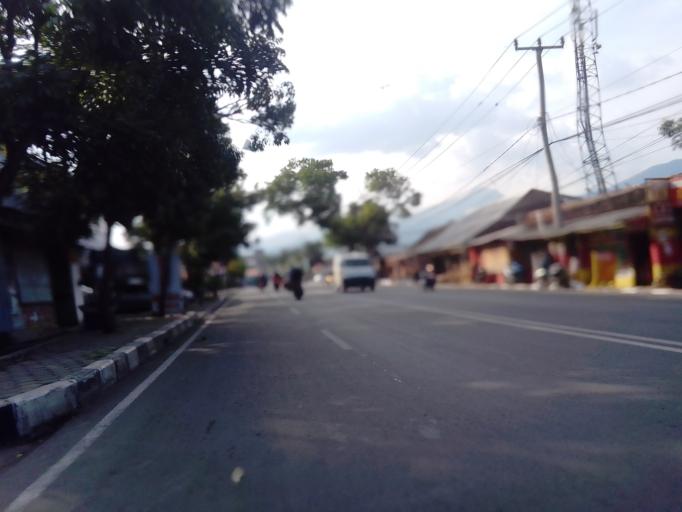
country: ID
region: West Java
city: Cileunyi
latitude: -6.9231
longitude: 107.7100
